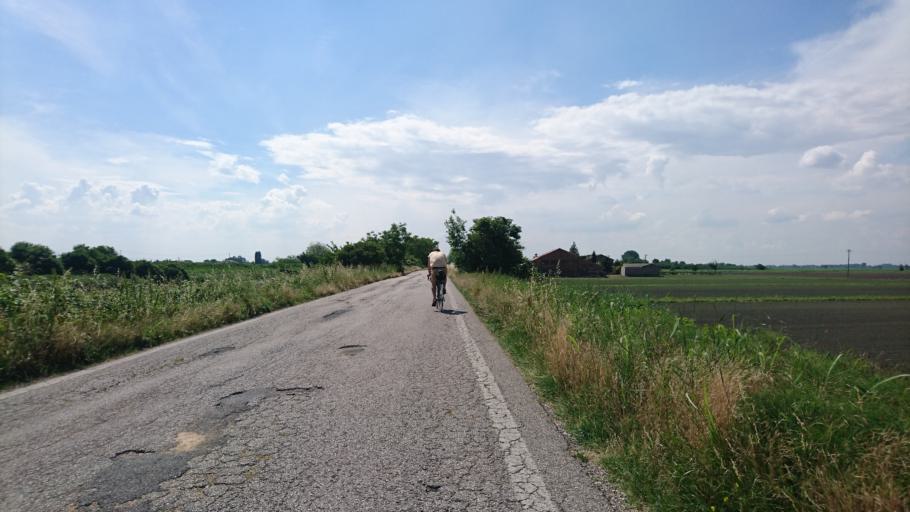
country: IT
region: Veneto
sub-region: Provincia di Rovigo
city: Ceneselli
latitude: 45.0727
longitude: 11.3474
